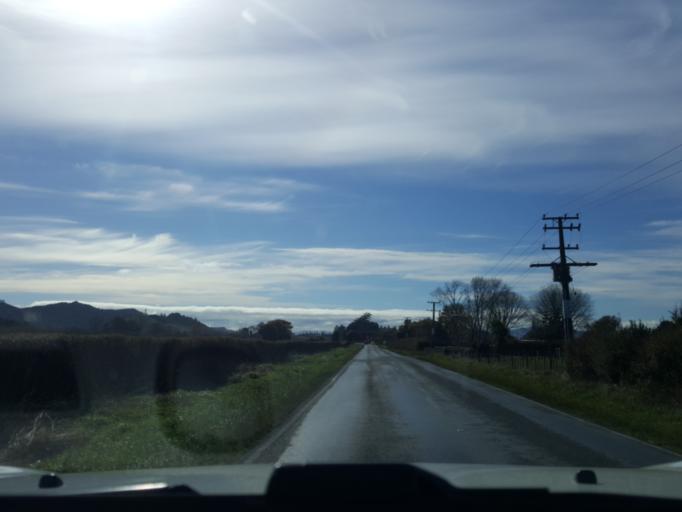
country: NZ
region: Waikato
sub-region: Waikato District
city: Ngaruawahia
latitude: -37.6047
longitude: 175.1991
